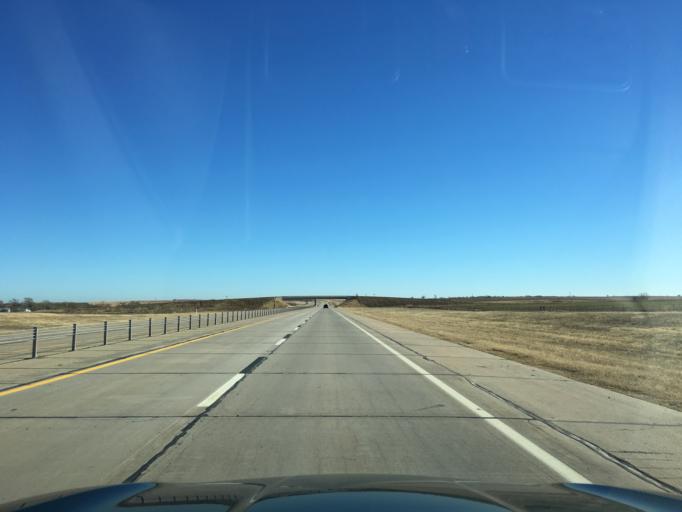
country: US
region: Oklahoma
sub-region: Noble County
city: Perry
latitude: 36.3978
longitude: -97.2339
